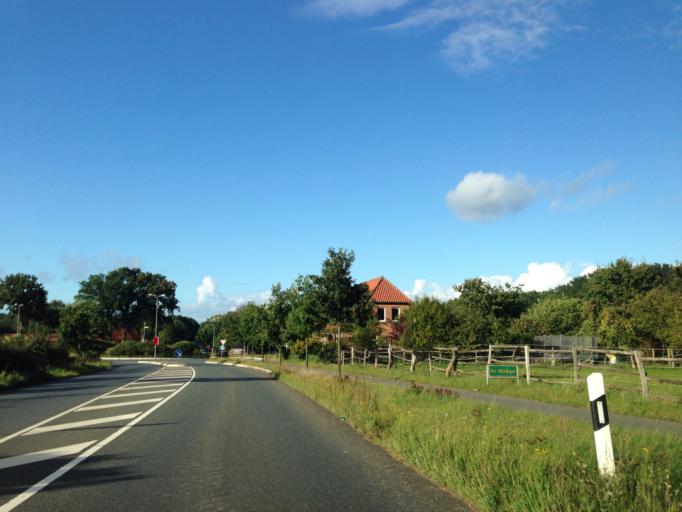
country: DE
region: Lower Saxony
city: Melbeck
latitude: 53.2067
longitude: 10.4053
